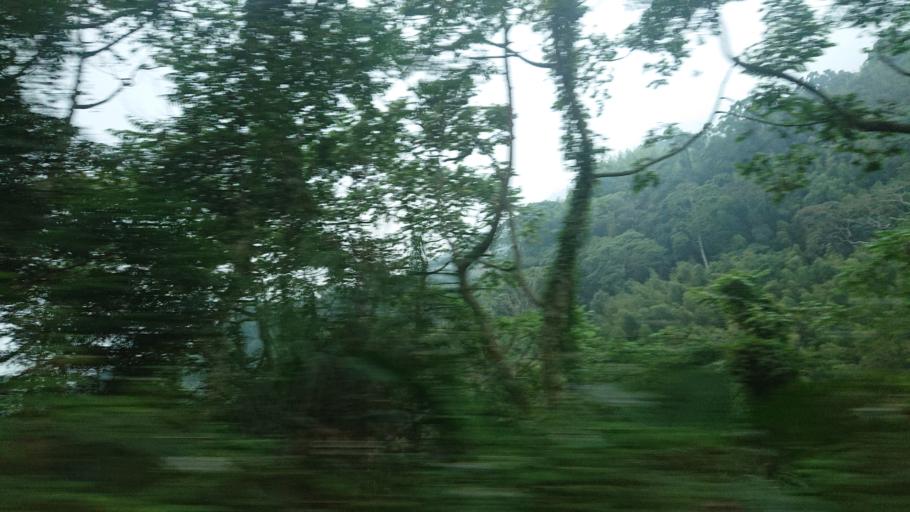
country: TW
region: Taiwan
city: Lugu
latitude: 23.6046
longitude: 120.7126
